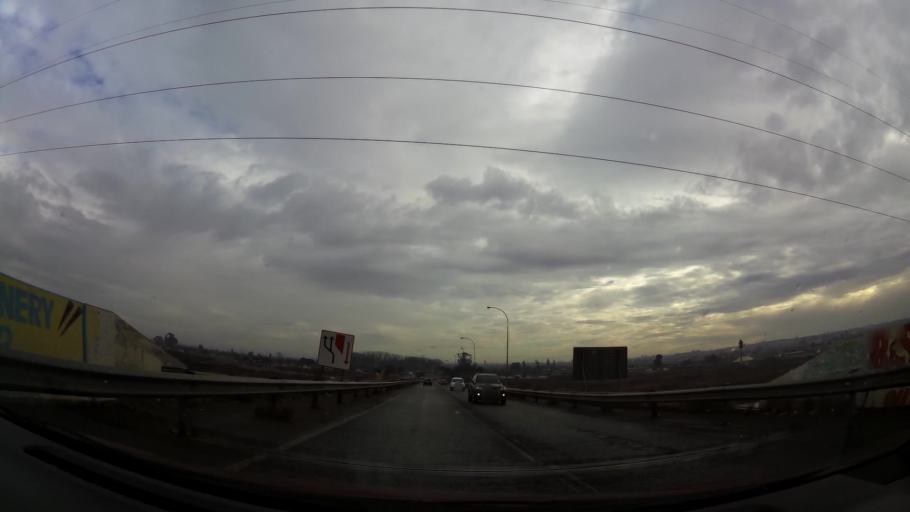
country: ZA
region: Gauteng
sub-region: City of Johannesburg Metropolitan Municipality
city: Soweto
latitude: -26.2939
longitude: 27.8459
